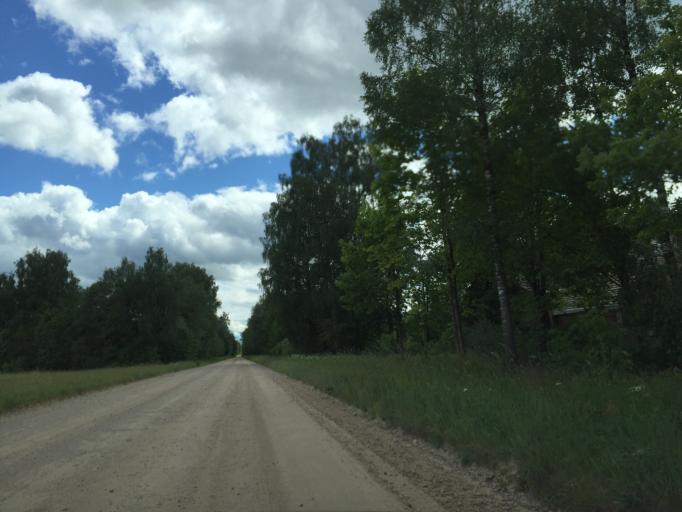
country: LV
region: Lecava
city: Iecava
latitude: 56.5508
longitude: 24.3585
